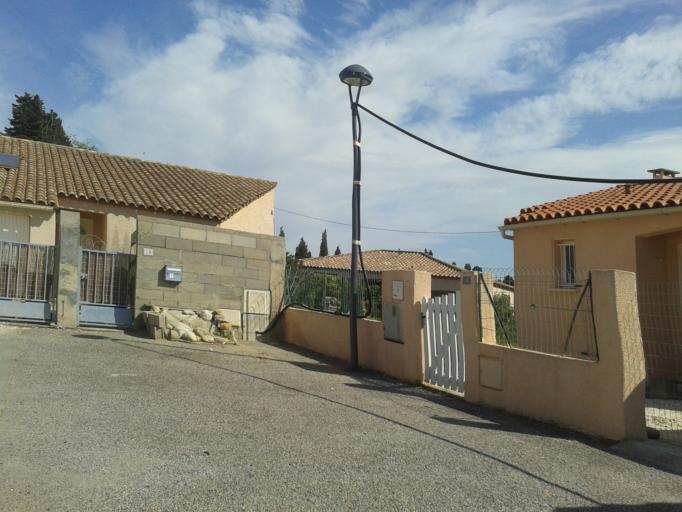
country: FR
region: Languedoc-Roussillon
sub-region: Departement des Pyrenees-Orientales
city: Corneilla-la-Riviere
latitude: 42.6999
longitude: 2.7294
